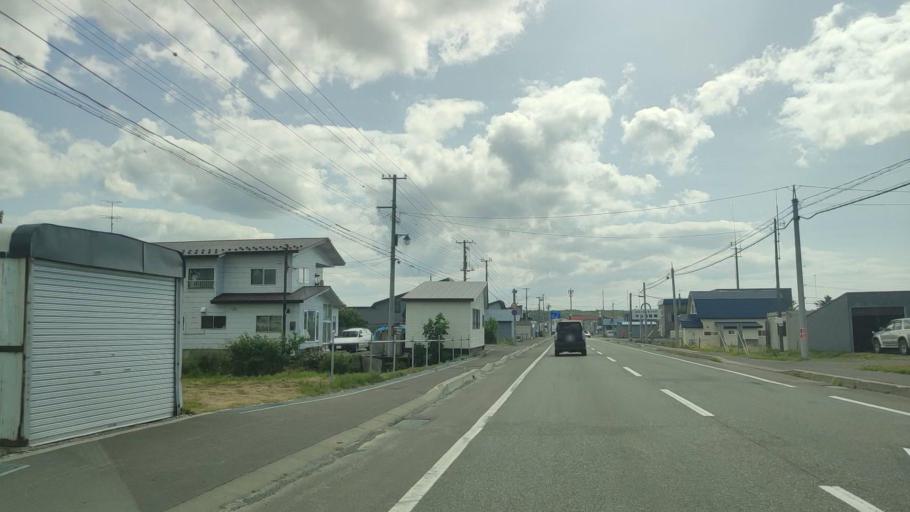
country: JP
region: Hokkaido
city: Makubetsu
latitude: 44.7284
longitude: 141.7989
